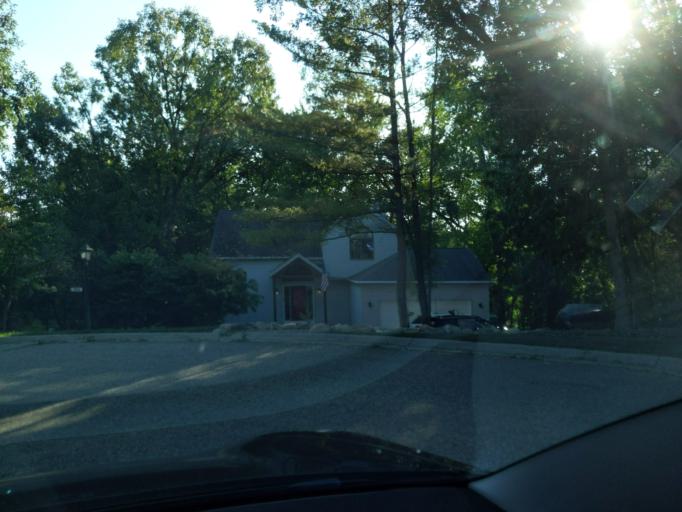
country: US
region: Michigan
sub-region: Livingston County
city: Whitmore Lake
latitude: 42.4458
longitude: -83.7499
